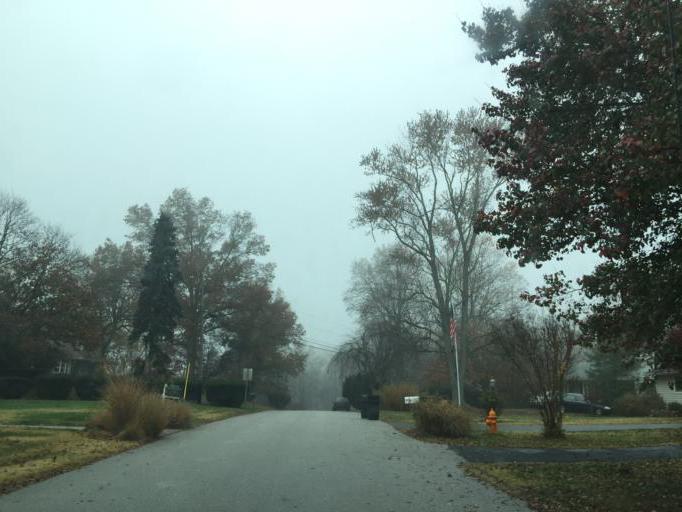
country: US
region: Maryland
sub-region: Howard County
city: Riverside
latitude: 39.1872
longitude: -76.8563
